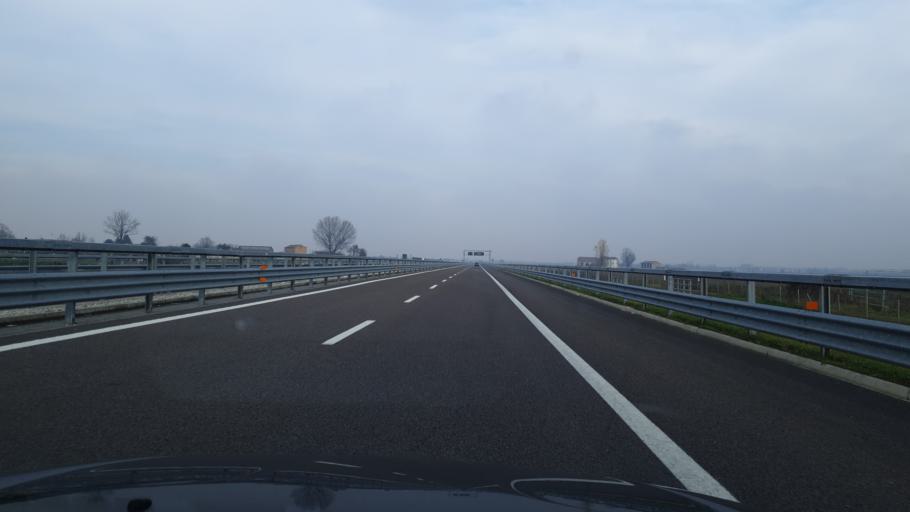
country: IT
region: Veneto
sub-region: Provincia di Padova
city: Saletto
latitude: 45.2446
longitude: 11.5643
